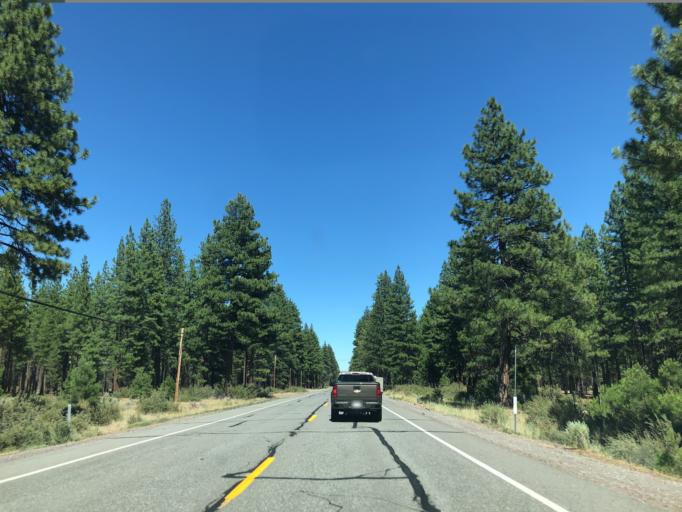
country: US
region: California
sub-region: Lassen County
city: Susanville
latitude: 40.4160
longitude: -120.7209
